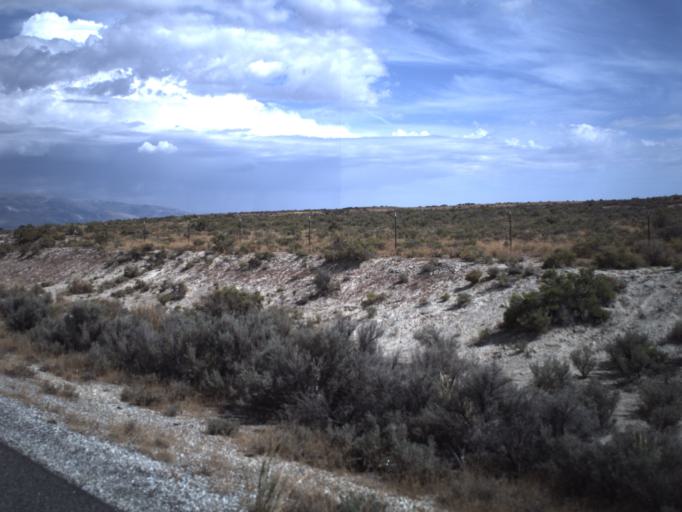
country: US
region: Idaho
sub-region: Cassia County
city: Burley
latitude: 41.6865
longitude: -113.5386
